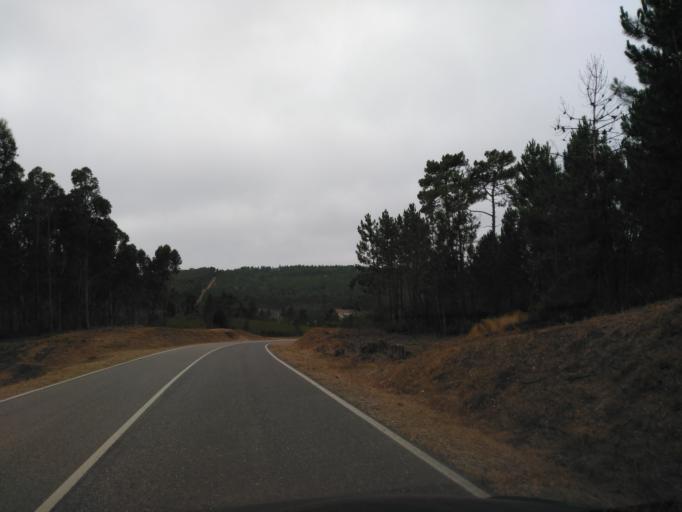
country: PT
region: Santarem
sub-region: Abrantes
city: Alferrarede
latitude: 39.5679
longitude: -8.1290
